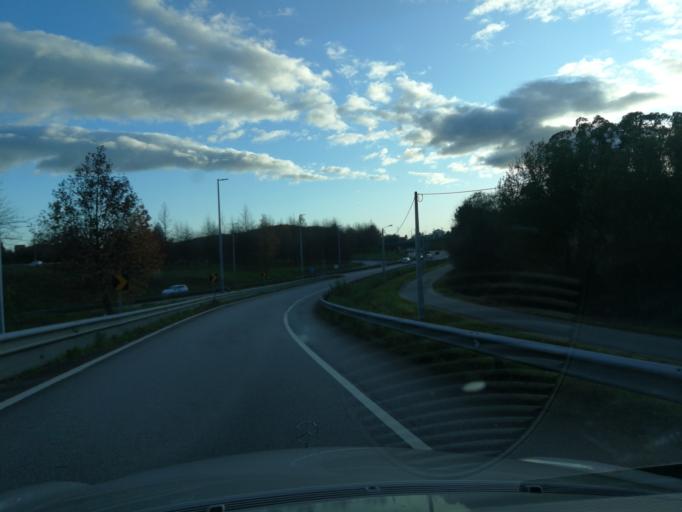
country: PT
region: Braga
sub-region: Barcelos
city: Vila Frescainha
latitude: 41.5354
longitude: -8.6384
